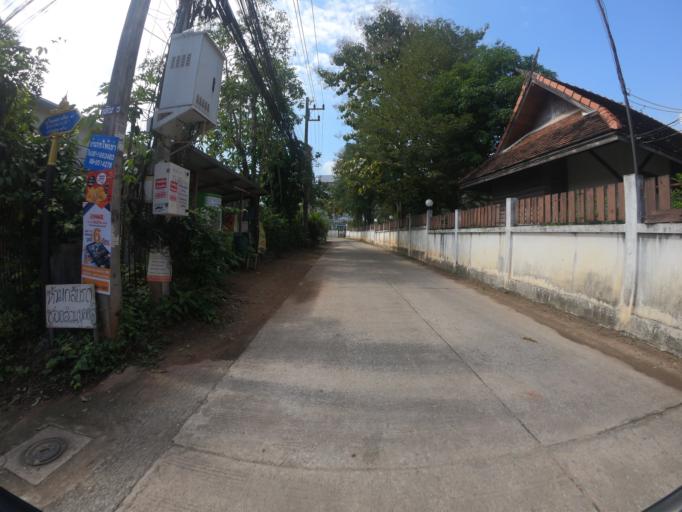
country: TH
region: Chiang Mai
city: Chiang Mai
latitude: 18.7896
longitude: 98.9532
